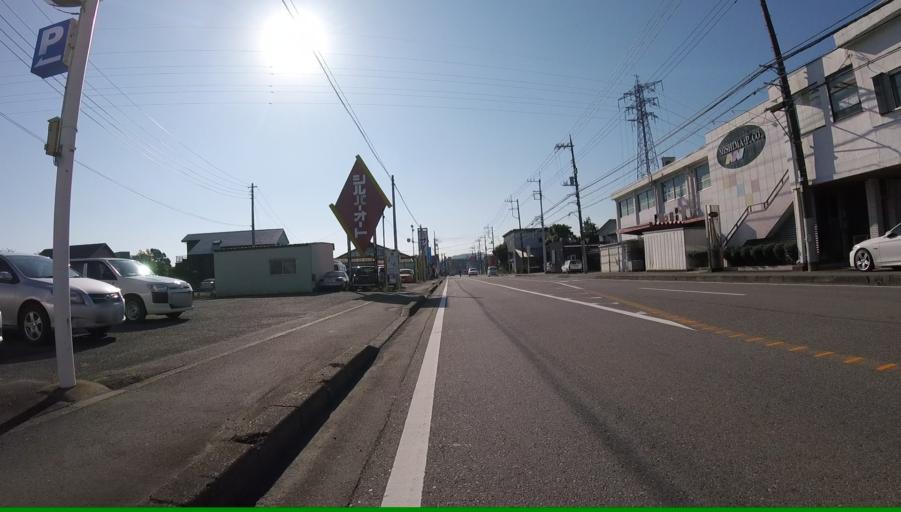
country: JP
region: Shizuoka
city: Mishima
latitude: 35.1069
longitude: 138.9158
